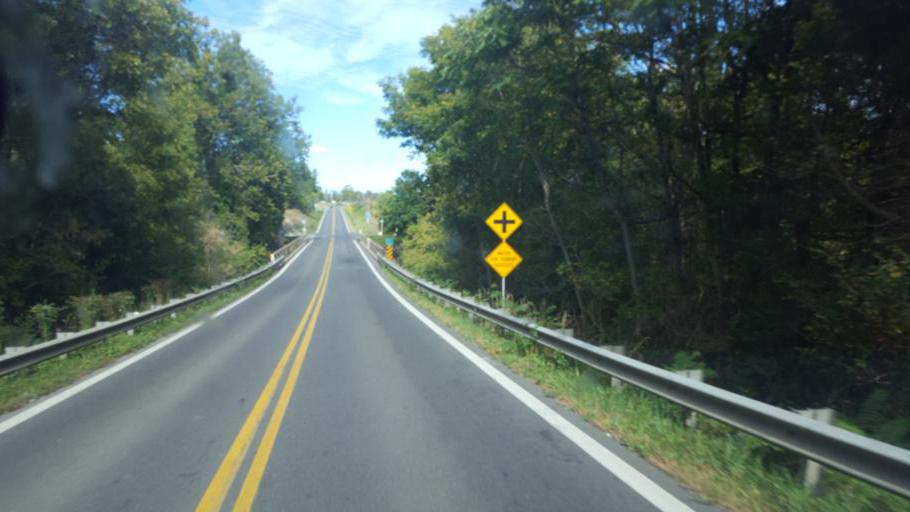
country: US
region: Virginia
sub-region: Page County
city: Luray
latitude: 38.7017
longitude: -78.4428
